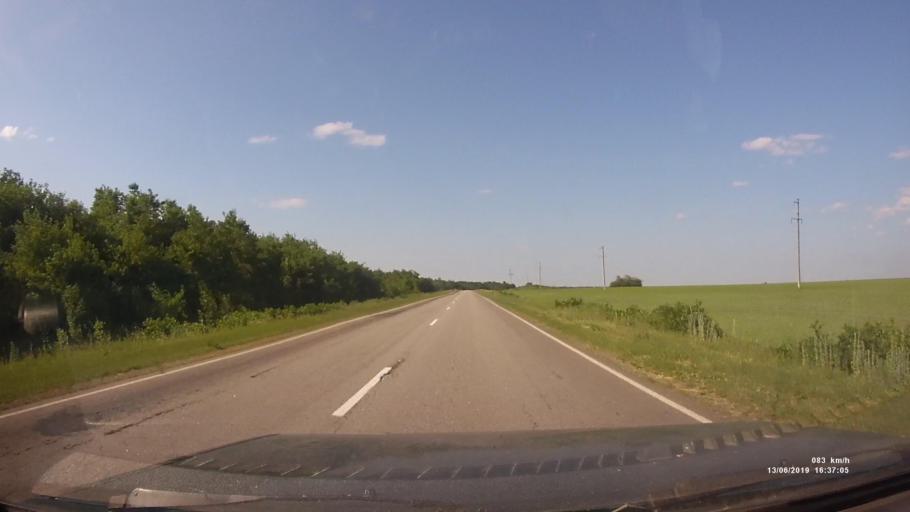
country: RU
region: Rostov
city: Kazanskaya
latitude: 49.9028
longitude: 41.3101
